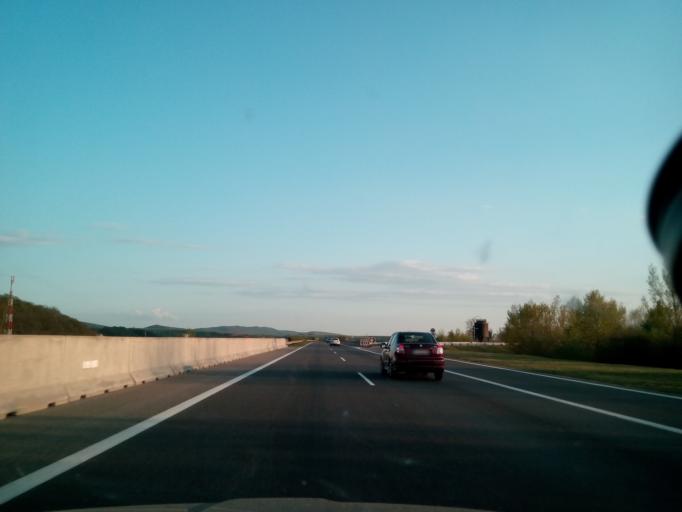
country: SK
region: Trenciansky
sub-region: Okres Nove Mesto nad Vahom
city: Nove Mesto nad Vahom
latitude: 48.6759
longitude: 17.8729
